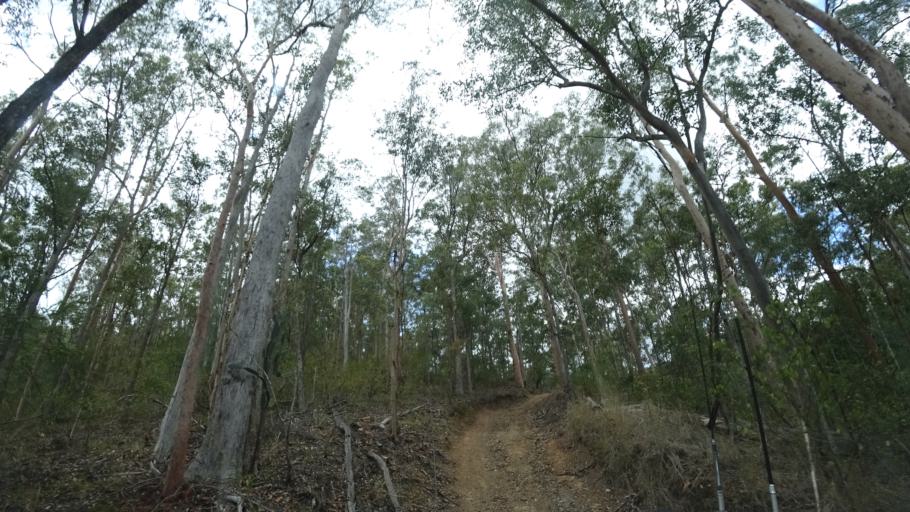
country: AU
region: Queensland
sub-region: Moreton Bay
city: Highvale
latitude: -27.4130
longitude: 152.7375
